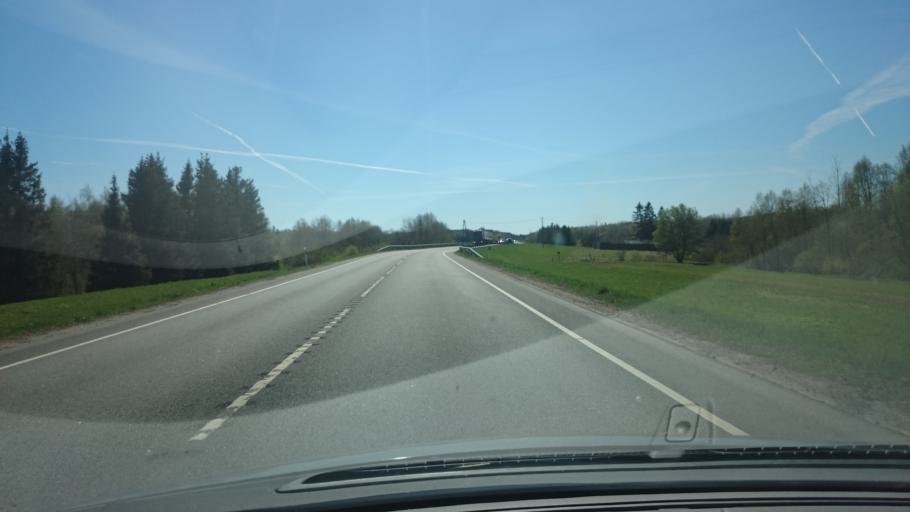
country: EE
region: Ida-Virumaa
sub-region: Narva-Joesuu linn
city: Narva-Joesuu
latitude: 59.3863
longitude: 27.9734
